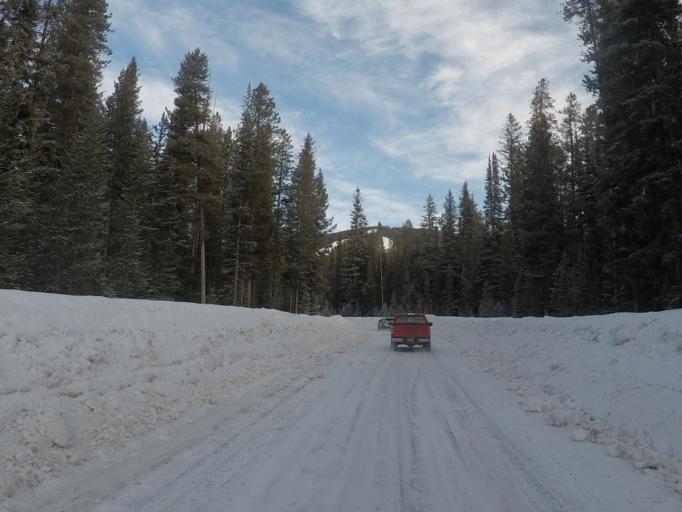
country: US
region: Montana
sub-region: Granite County
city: Philipsburg
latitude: 46.2426
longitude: -113.2434
